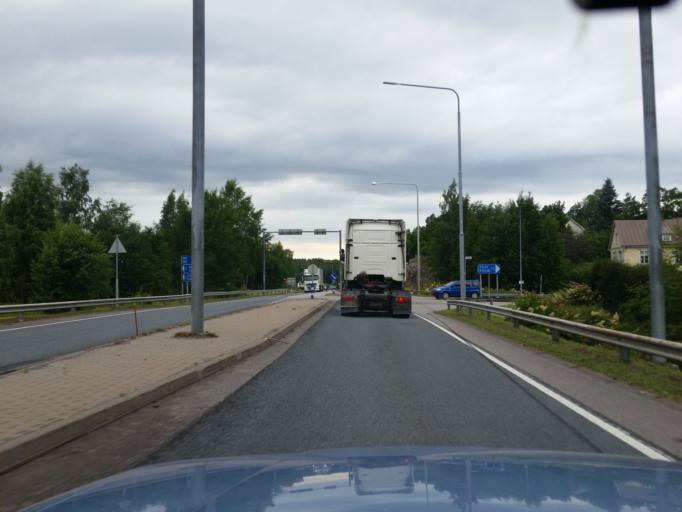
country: FI
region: Uusimaa
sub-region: Raaseporin
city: Ekenaes
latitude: 59.9836
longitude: 23.4258
